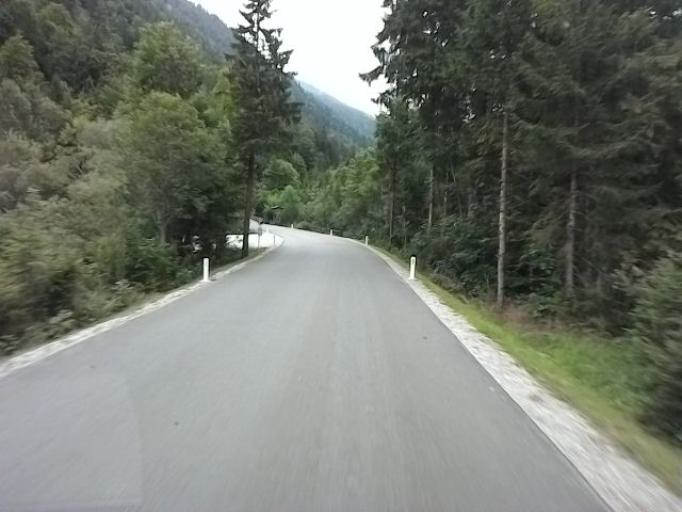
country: DE
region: Bavaria
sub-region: Upper Bavaria
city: Jachenau
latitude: 47.4683
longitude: 11.4763
